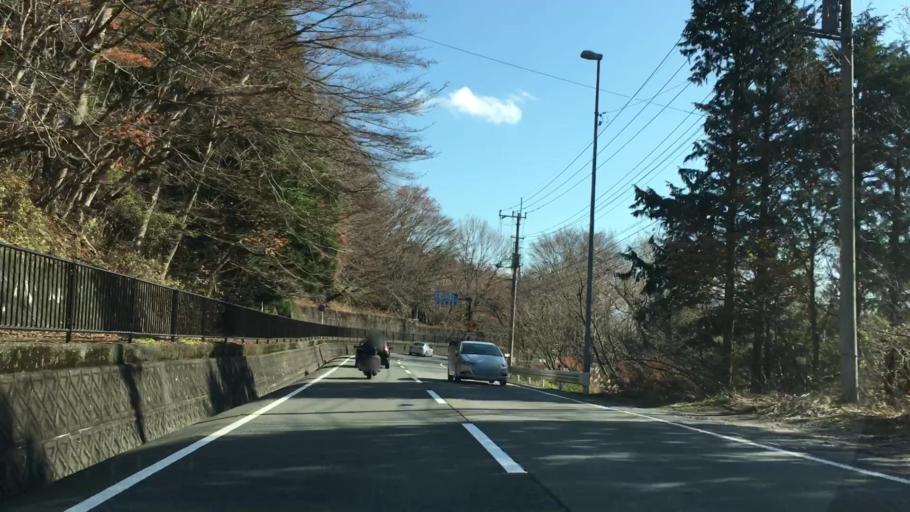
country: JP
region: Shizuoka
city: Gotemba
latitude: 35.3664
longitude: 138.8588
